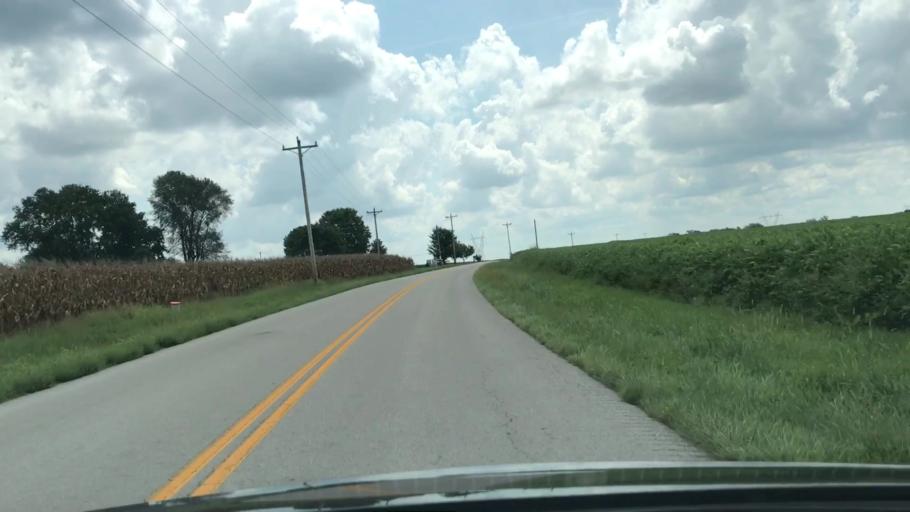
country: US
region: Kentucky
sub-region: Todd County
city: Elkton
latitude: 36.7801
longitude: -87.1215
